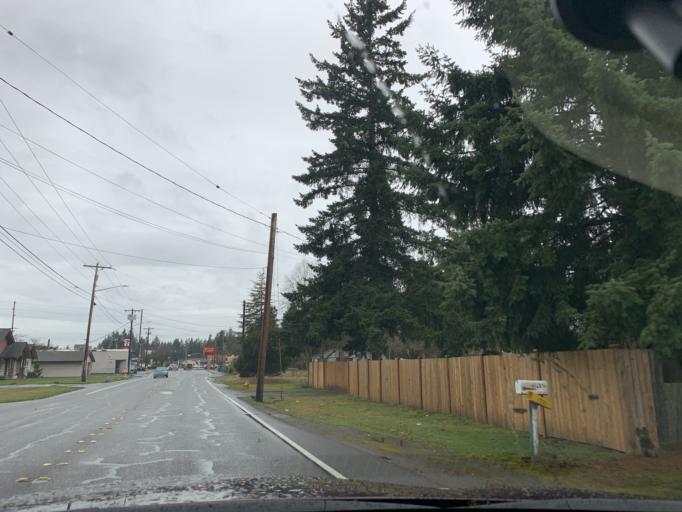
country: US
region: Washington
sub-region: Snohomish County
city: Marysville
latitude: 48.0872
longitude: -122.1695
